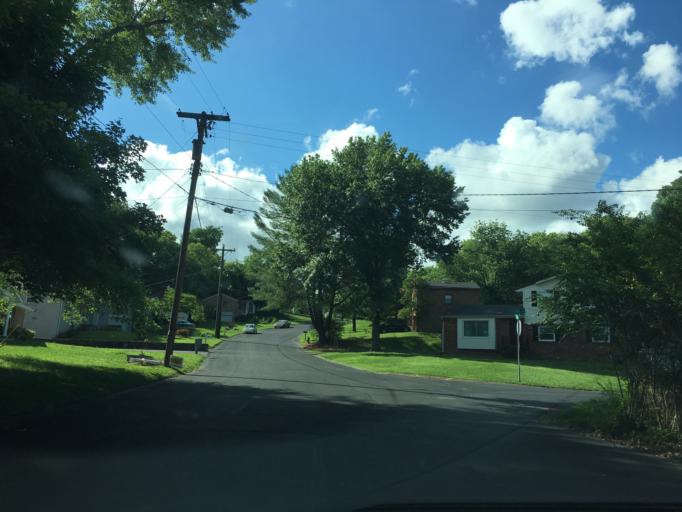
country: US
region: Tennessee
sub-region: Davidson County
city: Oak Hill
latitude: 36.0909
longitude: -86.7229
